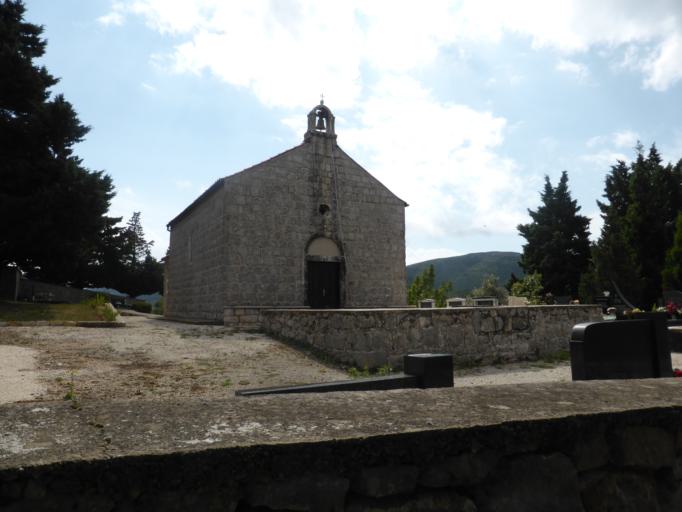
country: BA
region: Federation of Bosnia and Herzegovina
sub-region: Hercegovacko-Bosanski Kanton
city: Neum
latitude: 42.8891
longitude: 17.4992
